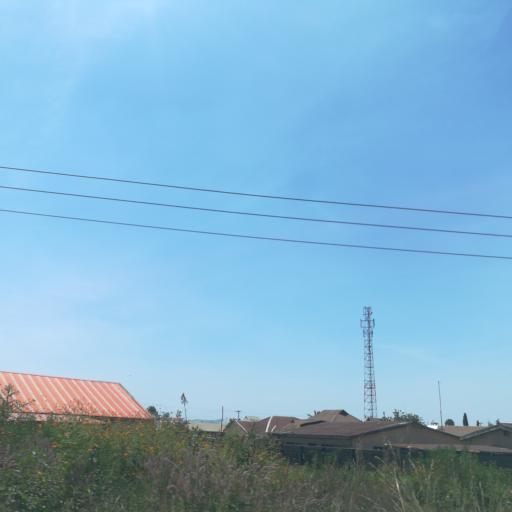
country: NG
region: Plateau
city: Bukuru
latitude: 9.7859
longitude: 8.8792
